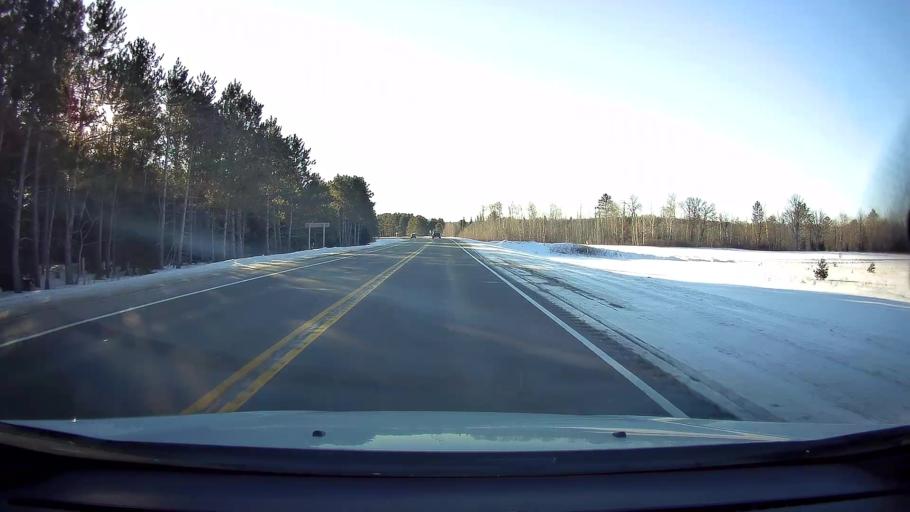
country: US
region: Wisconsin
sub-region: Sawyer County
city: Hayward
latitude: 45.9928
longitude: -91.5932
